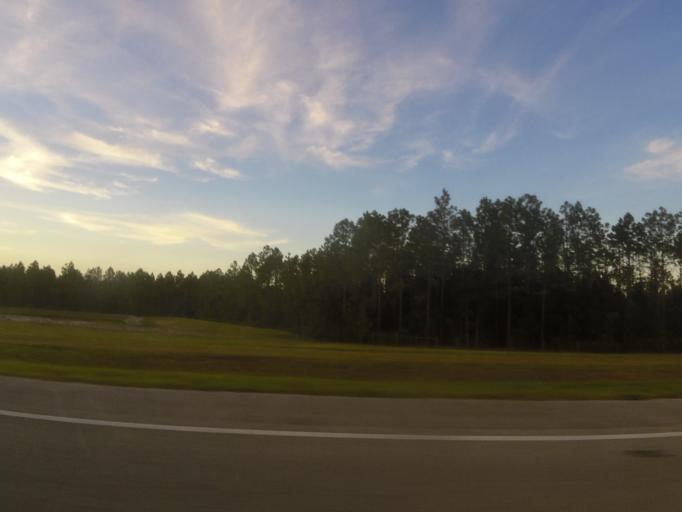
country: US
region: Florida
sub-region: Saint Johns County
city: Palm Valley
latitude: 30.1141
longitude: -81.4392
